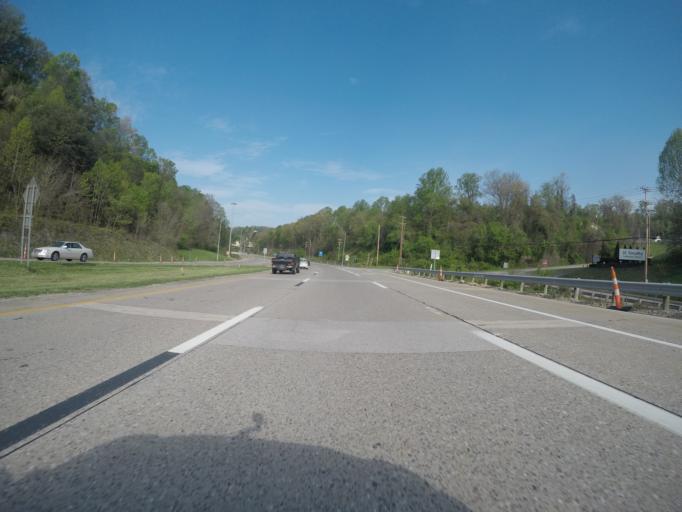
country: US
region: West Virginia
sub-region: Kanawha County
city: South Charleston
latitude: 38.3432
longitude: -81.6708
